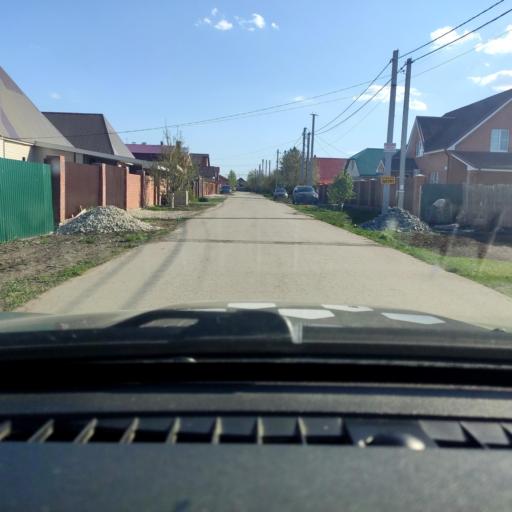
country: RU
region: Samara
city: Tol'yatti
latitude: 53.5638
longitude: 49.3784
